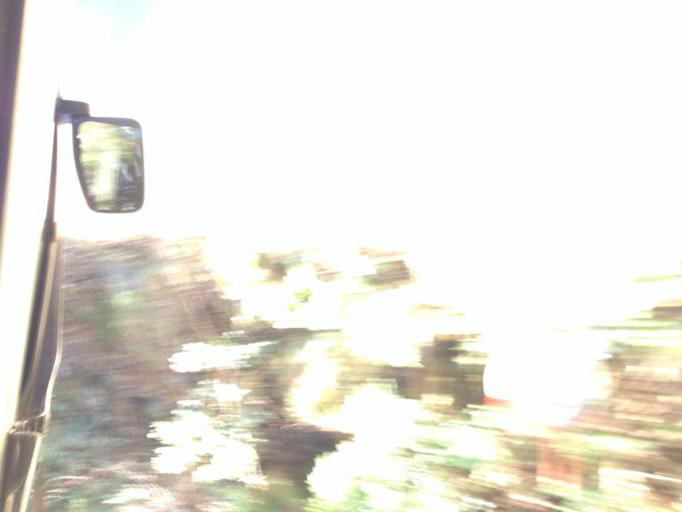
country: JP
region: Gifu
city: Mitake
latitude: 35.6092
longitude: 137.1890
